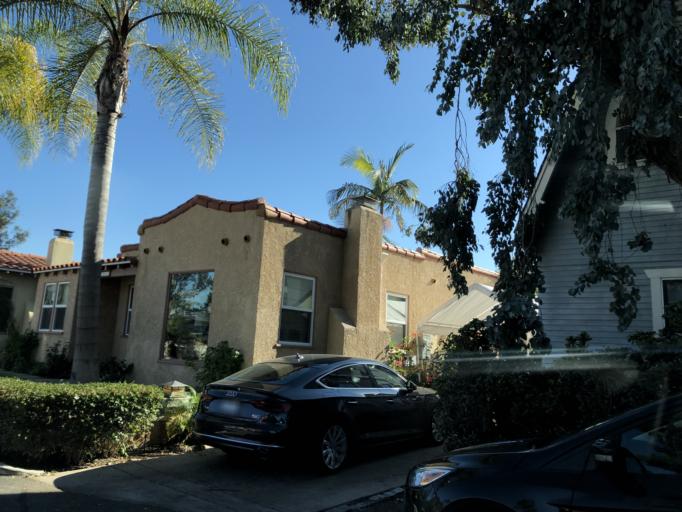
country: US
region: California
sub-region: San Diego County
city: San Diego
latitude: 32.7324
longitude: -117.1301
